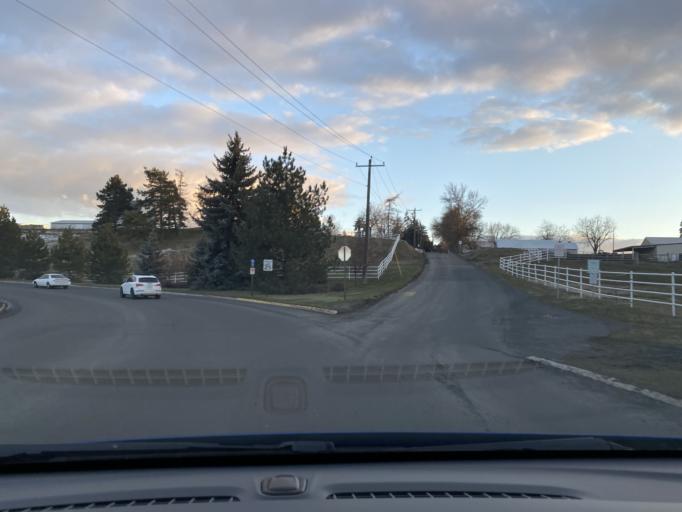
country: US
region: Idaho
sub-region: Latah County
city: Moscow
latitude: 46.7313
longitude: -117.0246
